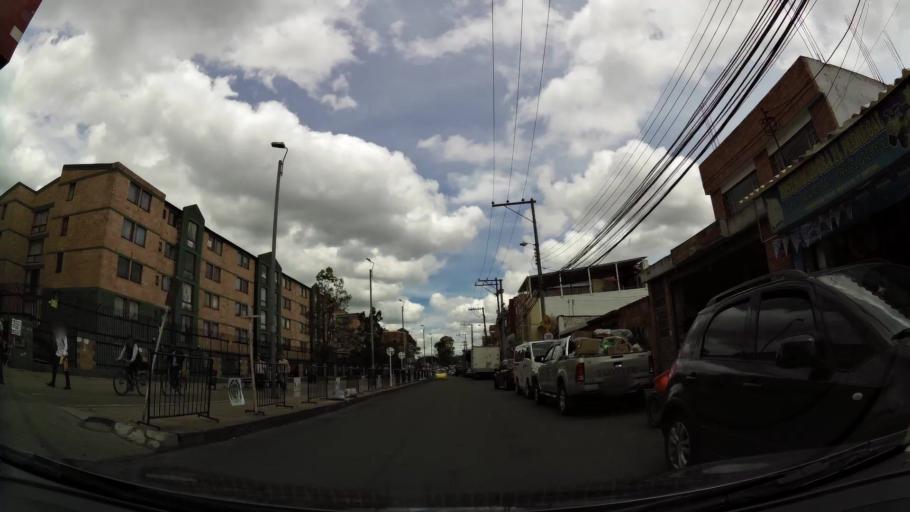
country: CO
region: Cundinamarca
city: Funza
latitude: 4.7026
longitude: -74.1173
